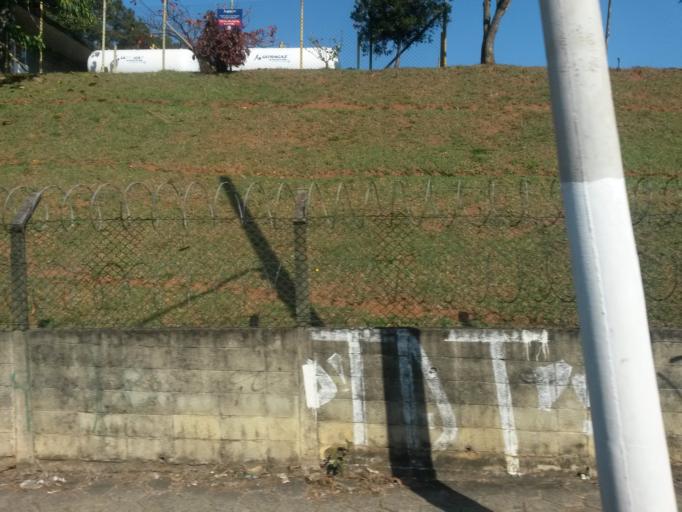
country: BR
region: Sao Paulo
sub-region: Sao Bernardo Do Campo
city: Sao Bernardo do Campo
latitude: -23.7003
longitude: -46.5634
